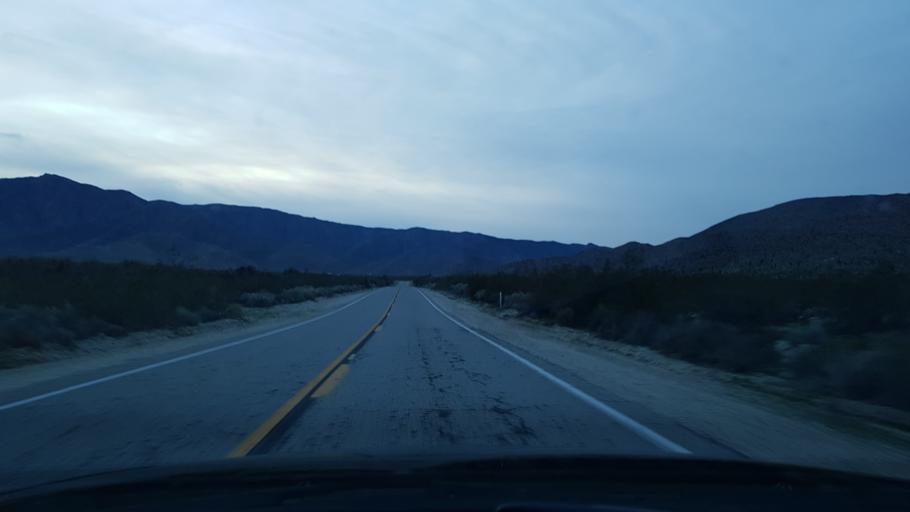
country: US
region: California
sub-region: San Diego County
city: Pine Valley
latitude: 32.9762
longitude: -116.3607
